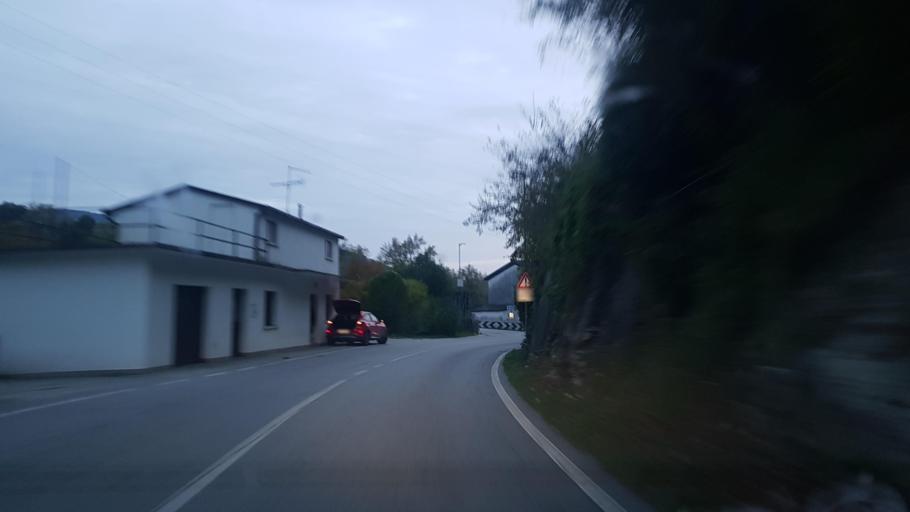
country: IT
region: Friuli Venezia Giulia
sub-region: Provincia di Udine
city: Forgaria nel Friuli
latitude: 46.2123
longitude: 12.9555
